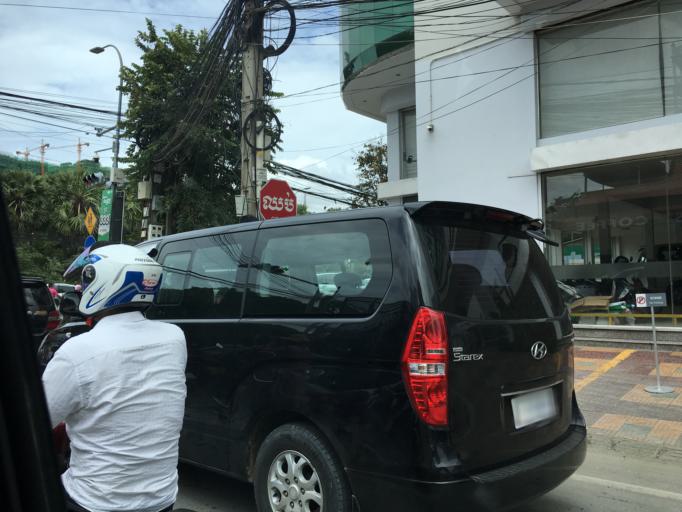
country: KH
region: Phnom Penh
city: Phnom Penh
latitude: 11.5346
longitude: 104.9236
